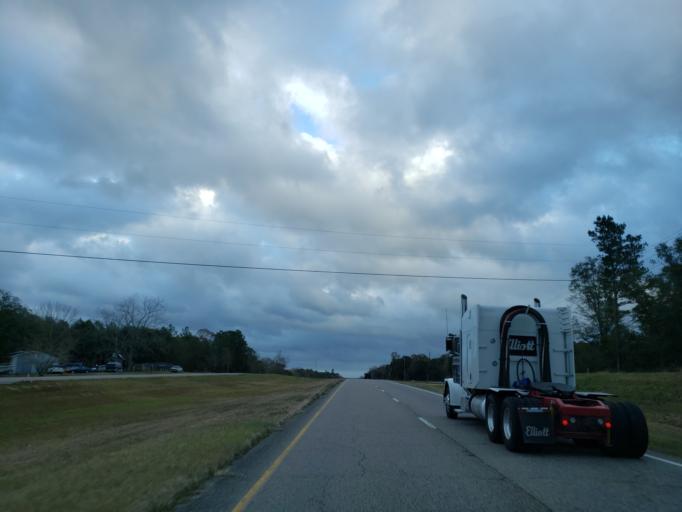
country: US
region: Mississippi
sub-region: George County
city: Lucedale
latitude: 30.9144
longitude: -88.4911
